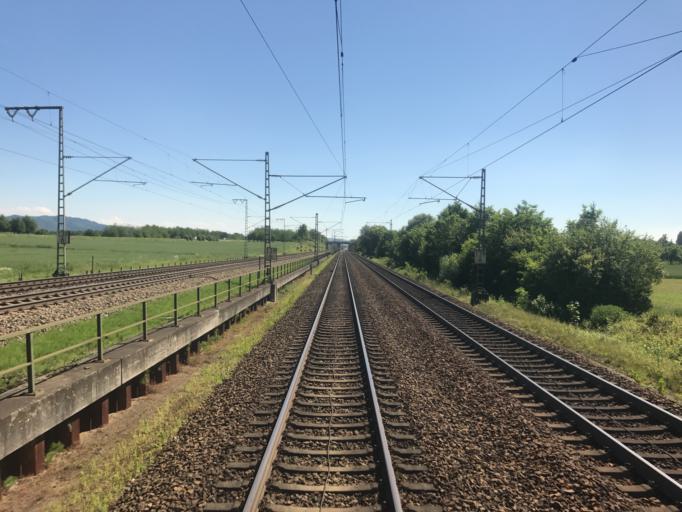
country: DE
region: Baden-Wuerttemberg
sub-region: Freiburg Region
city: Appenweier
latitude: 48.5274
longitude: 7.9691
